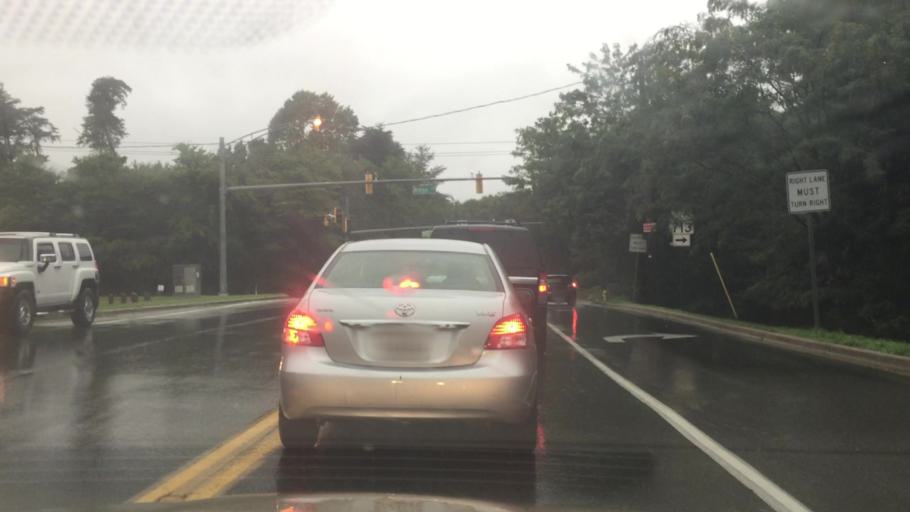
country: US
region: Maryland
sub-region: Anne Arundel County
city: Severn
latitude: 39.1419
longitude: -76.7279
